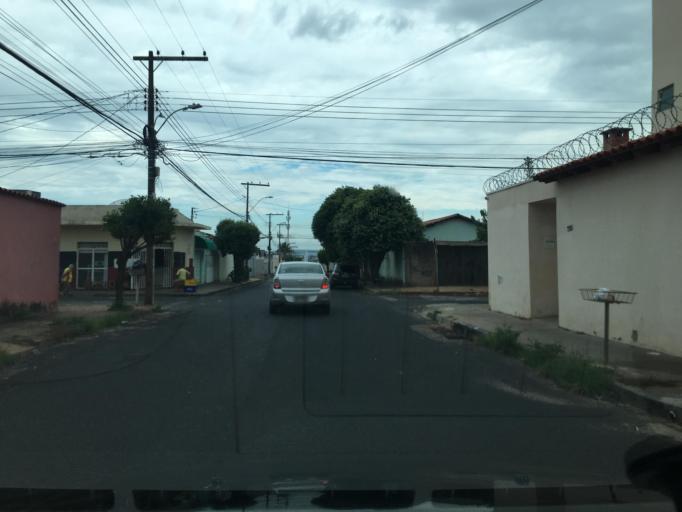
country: BR
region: Minas Gerais
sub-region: Uberlandia
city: Uberlandia
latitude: -18.9357
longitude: -48.3131
